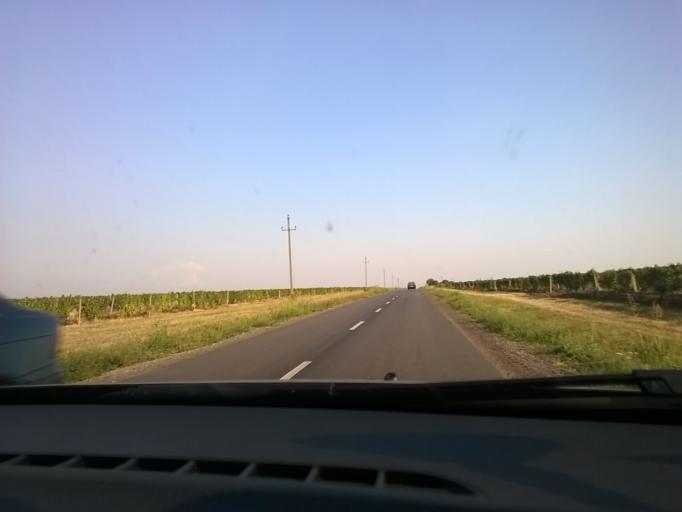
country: RS
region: Autonomna Pokrajina Vojvodina
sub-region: Juznobanatski Okrug
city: Vrsac
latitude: 45.1081
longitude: 21.3136
